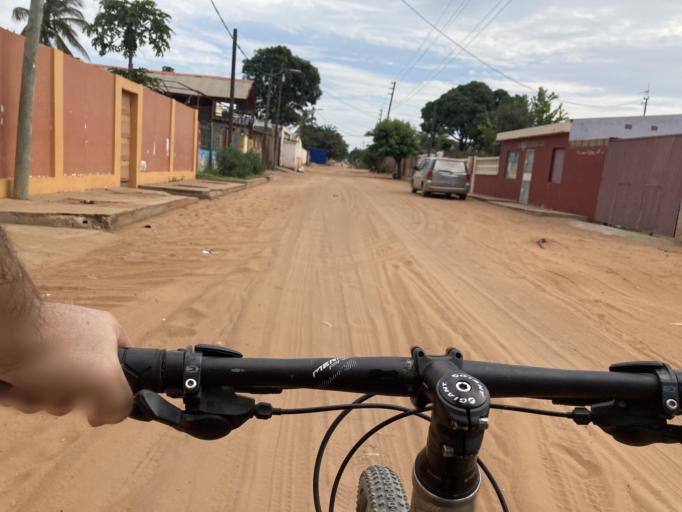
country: MZ
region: Maputo City
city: Maputo
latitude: -25.8921
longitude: 32.6082
